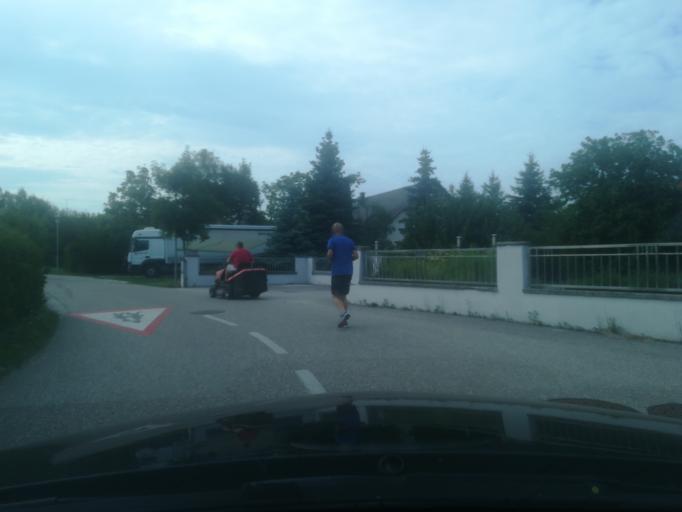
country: AT
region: Upper Austria
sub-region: Wels-Land
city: Marchtrenk
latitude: 48.1870
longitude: 14.1319
